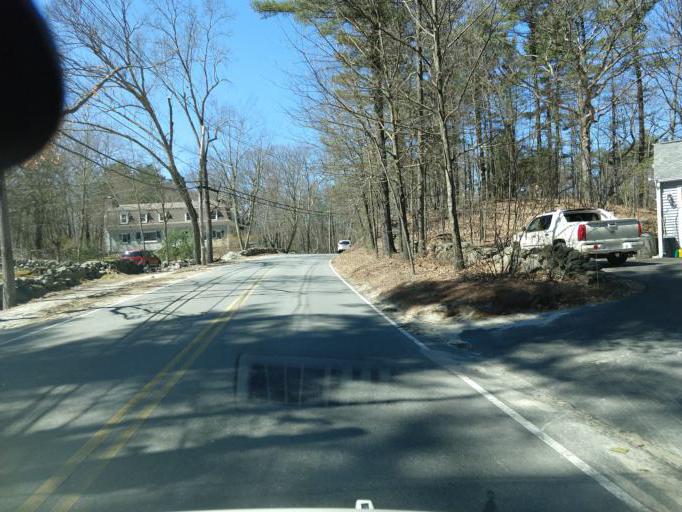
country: US
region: Massachusetts
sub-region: Middlesex County
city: Carlisle
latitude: 42.5355
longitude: -71.3486
